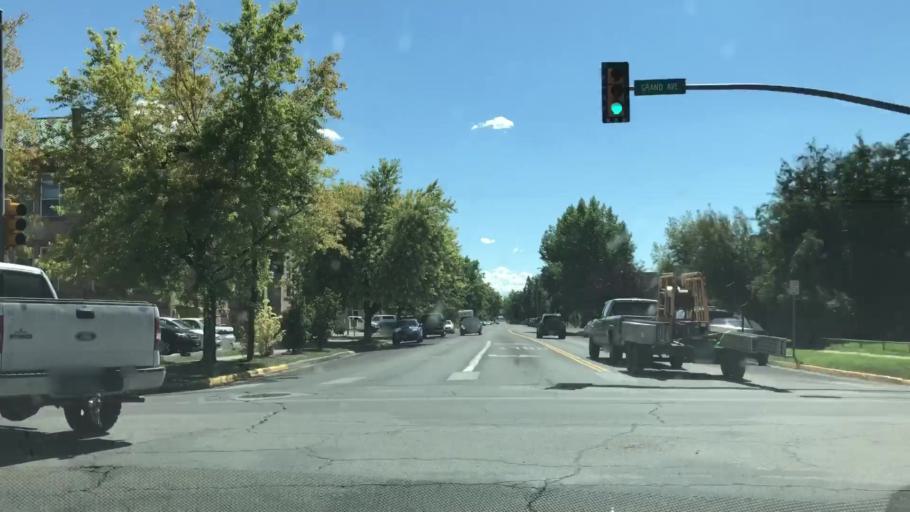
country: US
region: Wyoming
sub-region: Albany County
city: Laramie
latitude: 41.3106
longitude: -105.5857
